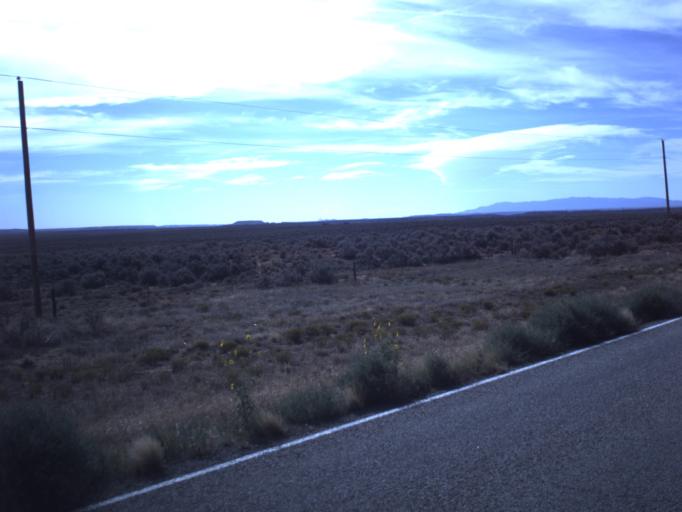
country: US
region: Utah
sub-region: San Juan County
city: Blanding
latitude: 37.4039
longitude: -109.3368
